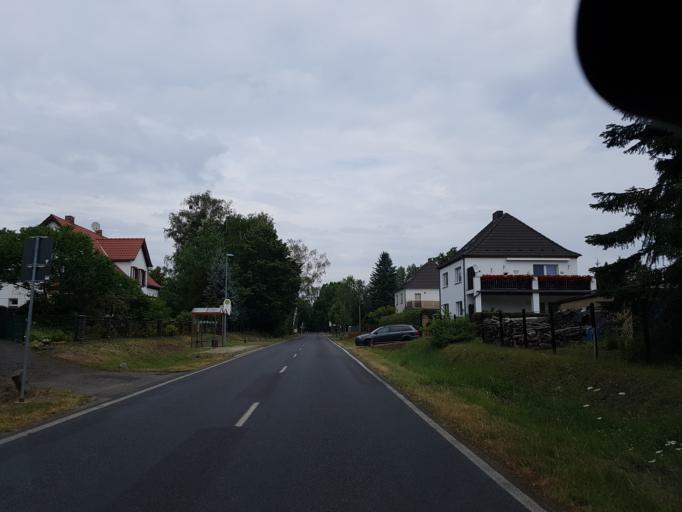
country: DE
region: Brandenburg
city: Schipkau
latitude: 51.5267
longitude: 13.8942
